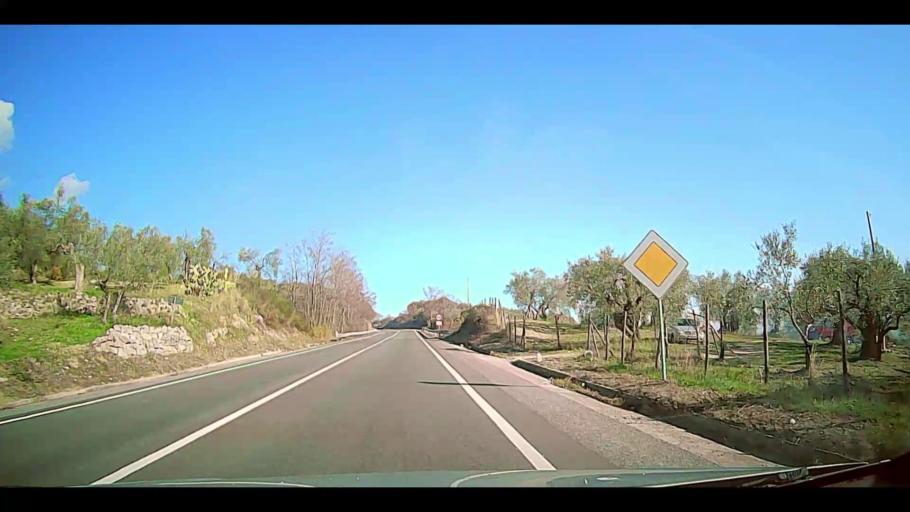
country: IT
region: Calabria
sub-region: Provincia di Crotone
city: Caccuri
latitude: 39.2131
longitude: 16.7967
